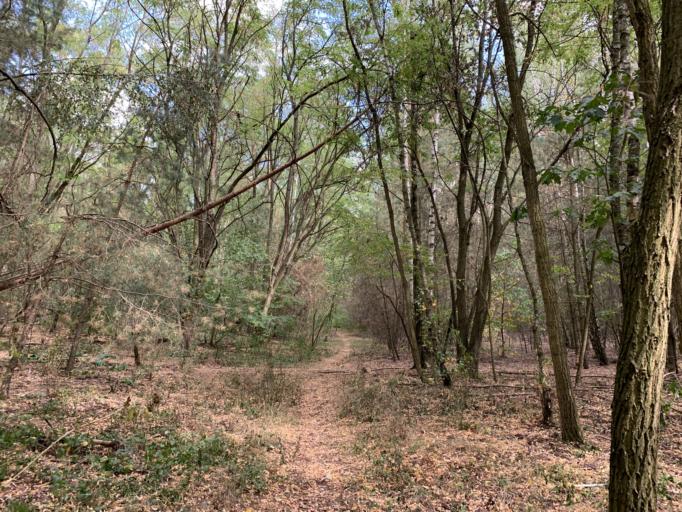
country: DE
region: Berlin
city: Nikolassee
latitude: 52.4091
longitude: 13.1849
